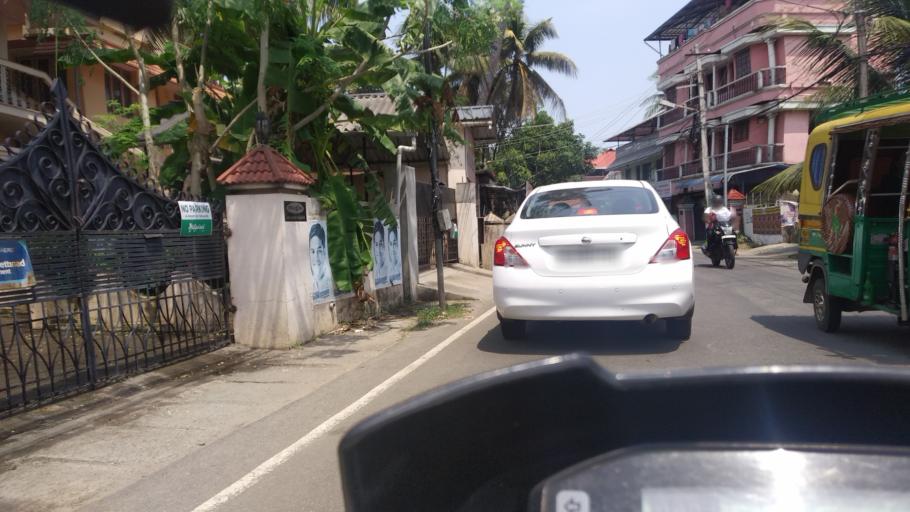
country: IN
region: Kerala
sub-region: Ernakulam
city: Cochin
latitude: 9.9611
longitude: 76.3010
